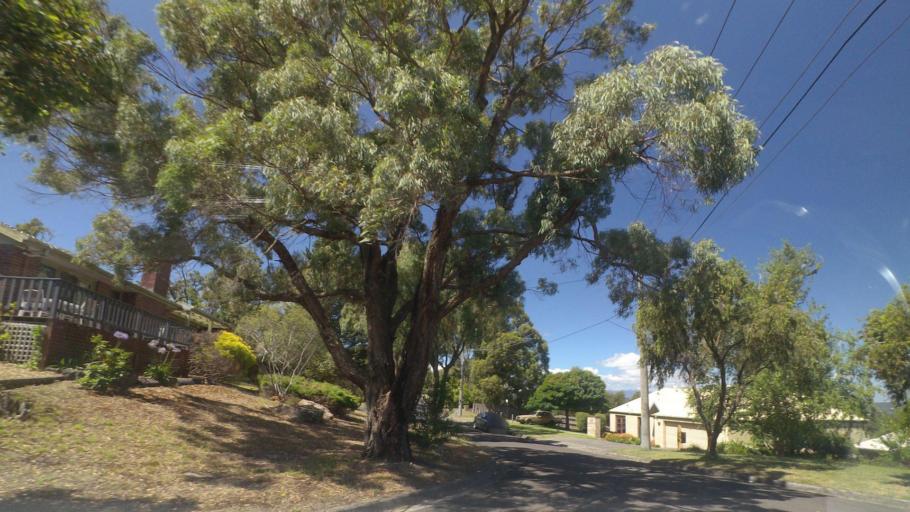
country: AU
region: Victoria
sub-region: Maroondah
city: Croydon Hills
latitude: -37.7778
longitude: 145.2785
